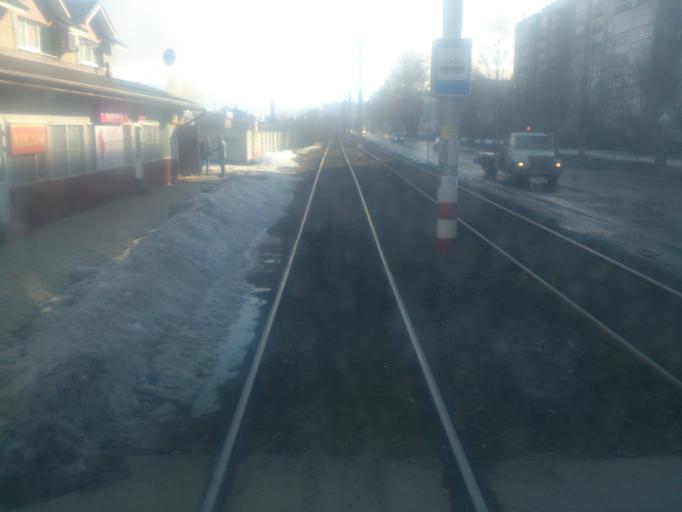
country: RU
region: Ulyanovsk
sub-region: Ulyanovskiy Rayon
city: Ulyanovsk
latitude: 54.2676
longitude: 48.2838
